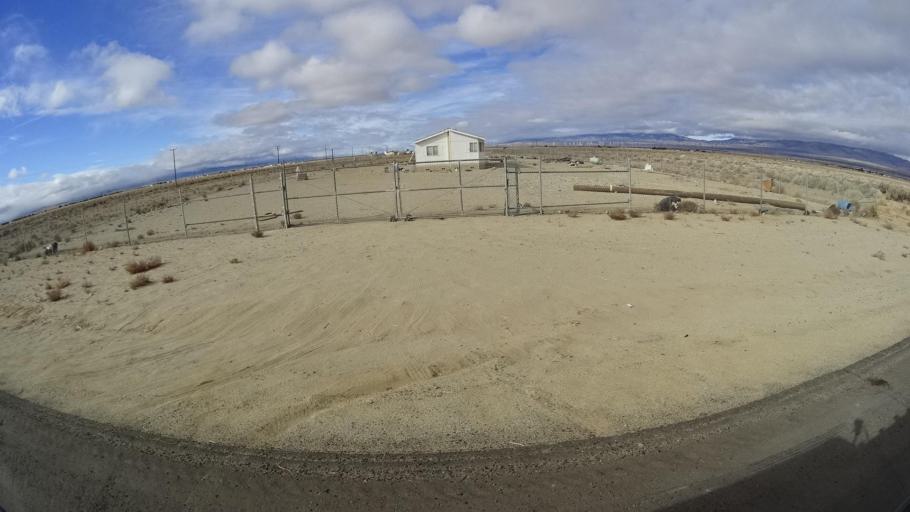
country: US
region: California
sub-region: Kern County
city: Rosamond
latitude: 34.8462
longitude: -118.2909
